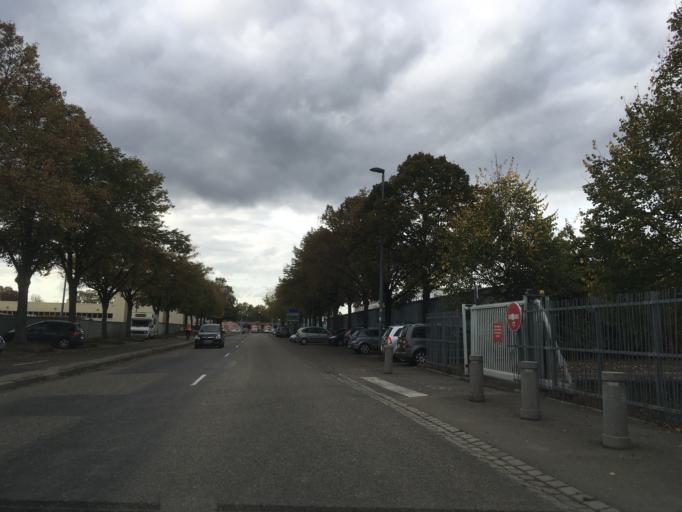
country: FR
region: Alsace
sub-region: Departement du Bas-Rhin
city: Strasbourg
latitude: 48.5641
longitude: 7.7412
